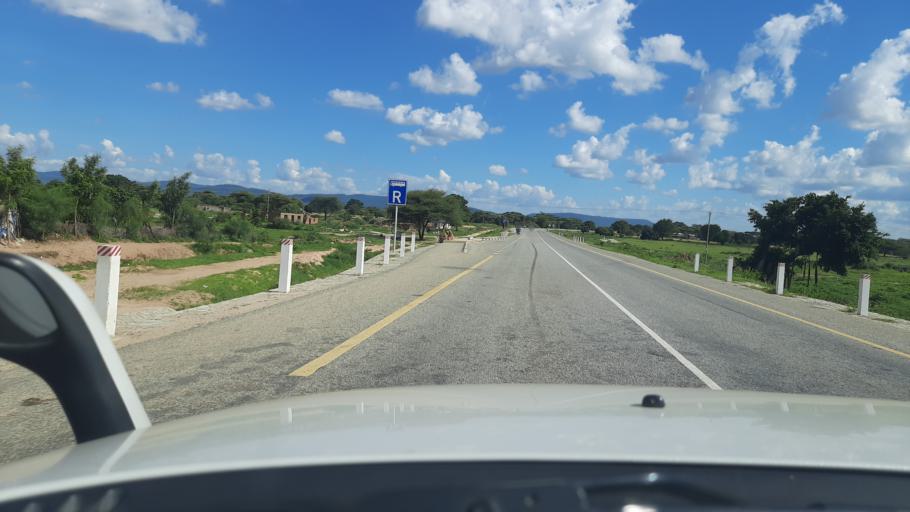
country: TZ
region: Dodoma
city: Kondoa
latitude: -5.1102
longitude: 35.8267
